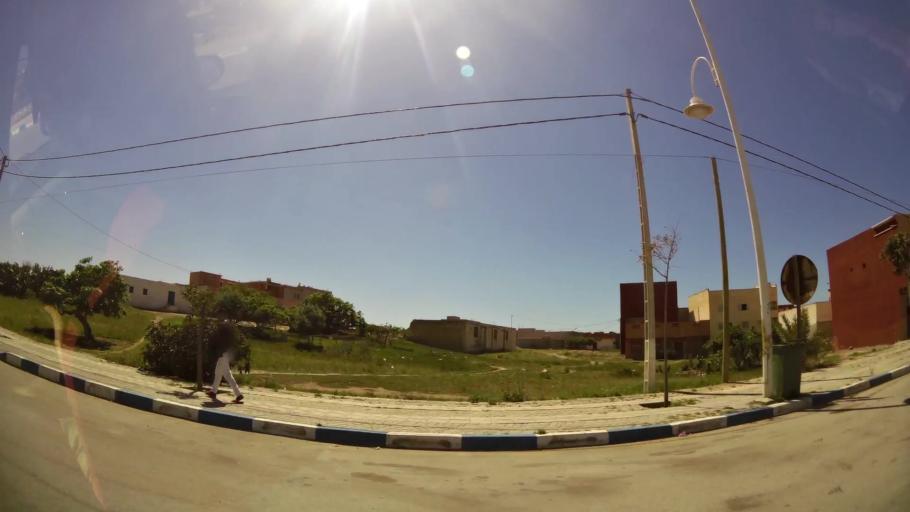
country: MA
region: Oriental
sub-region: Berkane-Taourirt
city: Madagh
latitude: 35.1333
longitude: -2.4247
